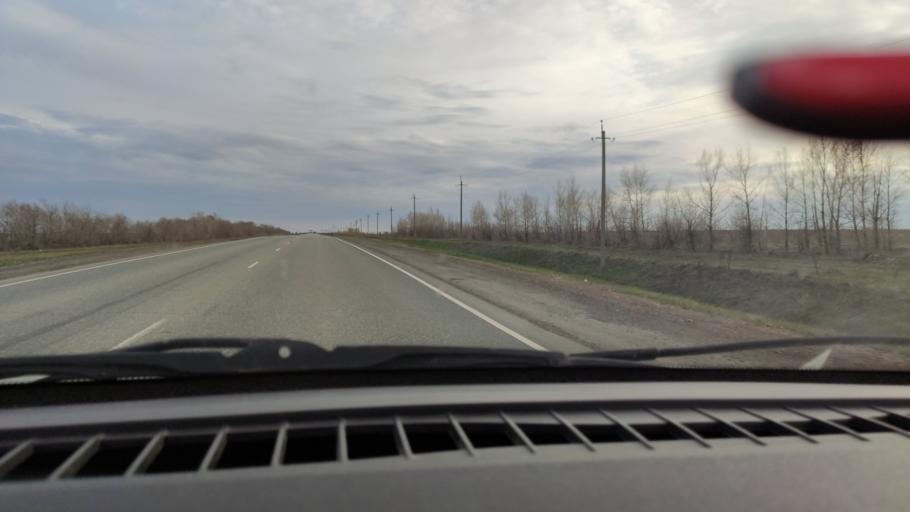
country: RU
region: Orenburg
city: Tatarskaya Kargala
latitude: 52.0101
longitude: 55.2033
